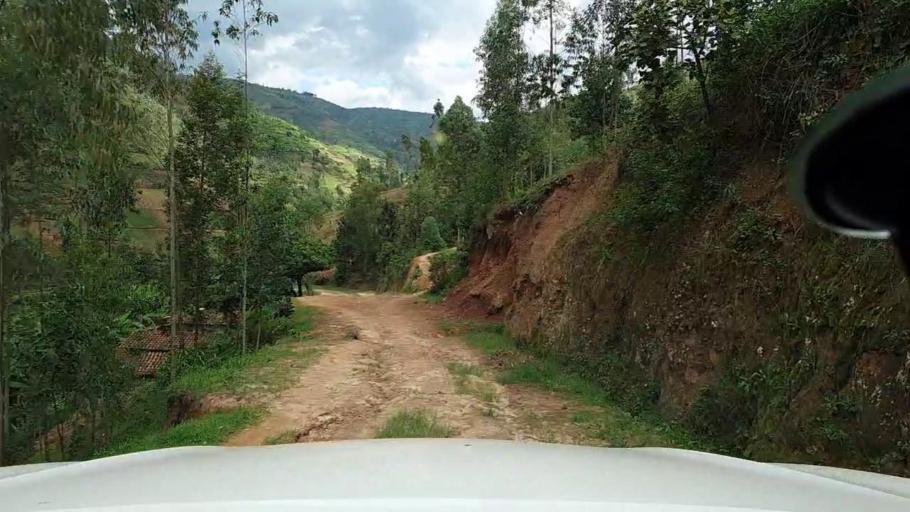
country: RW
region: Southern Province
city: Gitarama
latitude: -1.8157
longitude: 29.8006
